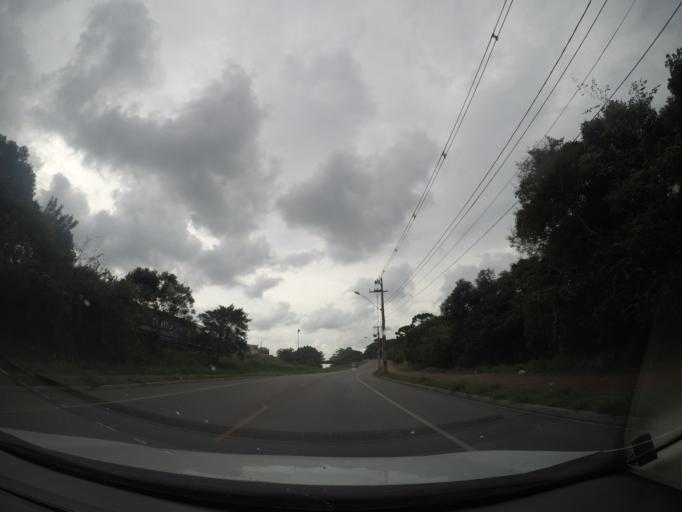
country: BR
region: Parana
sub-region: Sao Jose Dos Pinhais
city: Sao Jose dos Pinhais
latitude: -25.5466
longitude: -49.2438
